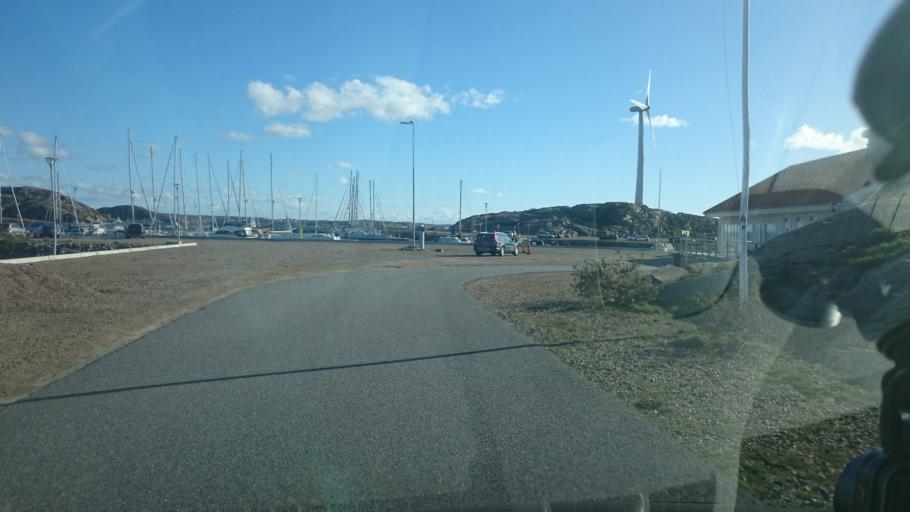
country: SE
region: Vaestra Goetaland
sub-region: Lysekils Kommun
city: Lysekil
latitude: 58.3160
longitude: 11.3953
